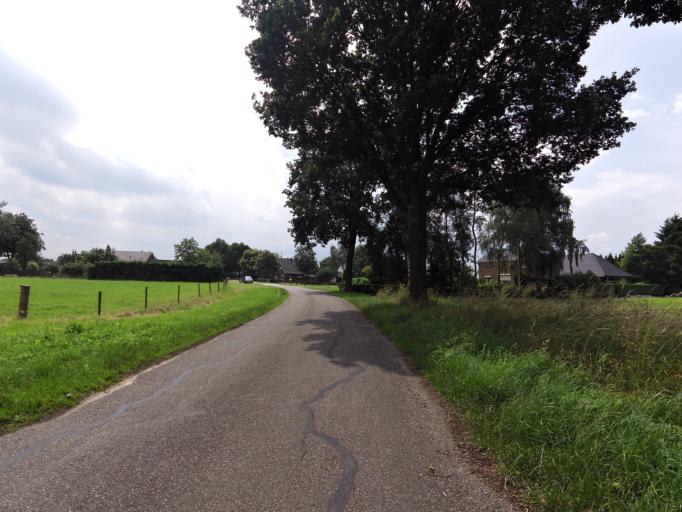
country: NL
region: Gelderland
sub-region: Gemeente Doesburg
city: Doesburg
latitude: 51.9251
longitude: 6.1703
